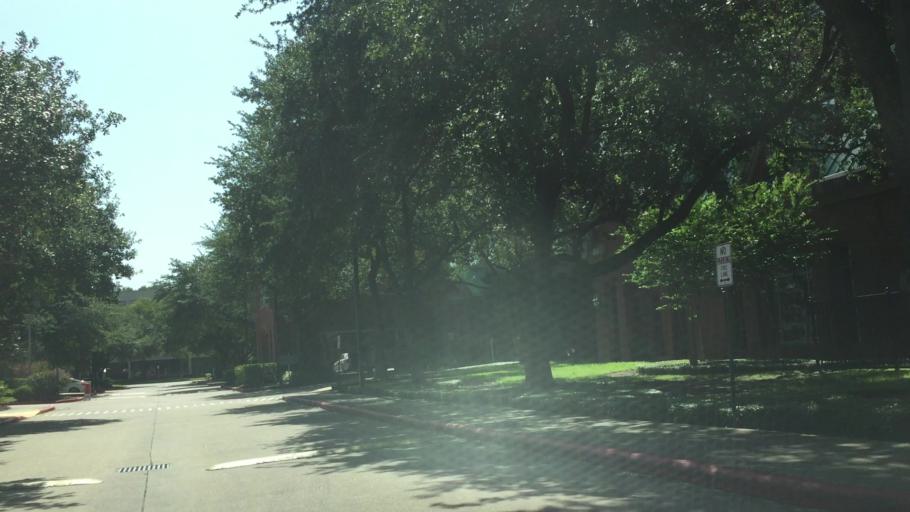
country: US
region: Texas
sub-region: Harris County
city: Hunters Creek Village
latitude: 29.7808
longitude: -95.4583
